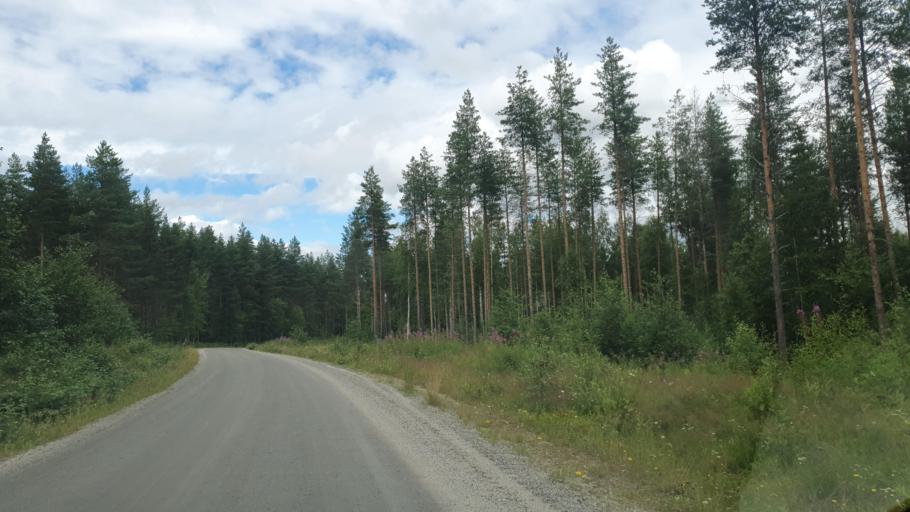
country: FI
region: Kainuu
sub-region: Kehys-Kainuu
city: Kuhmo
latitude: 64.0992
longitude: 29.4048
